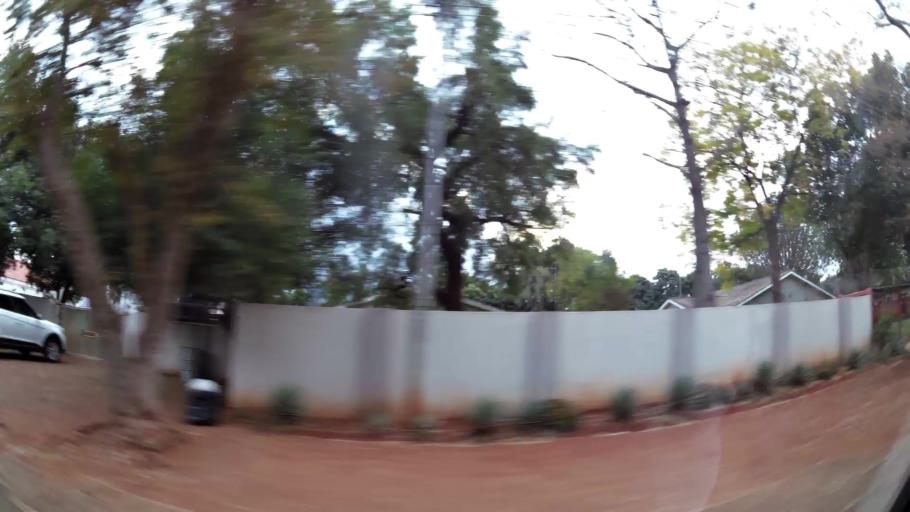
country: ZA
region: Limpopo
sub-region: Waterberg District Municipality
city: Mokopane
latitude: -24.1910
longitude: 28.9915
